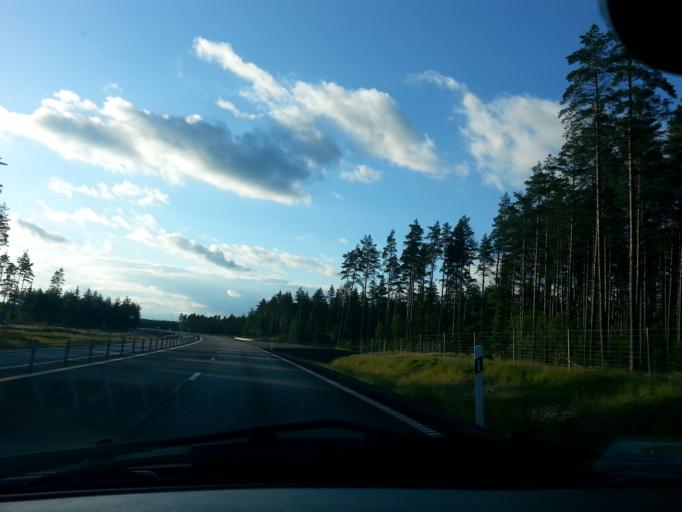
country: SE
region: Joenkoeping
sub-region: Gislaveds Kommun
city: Gislaved
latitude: 57.3081
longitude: 13.5770
